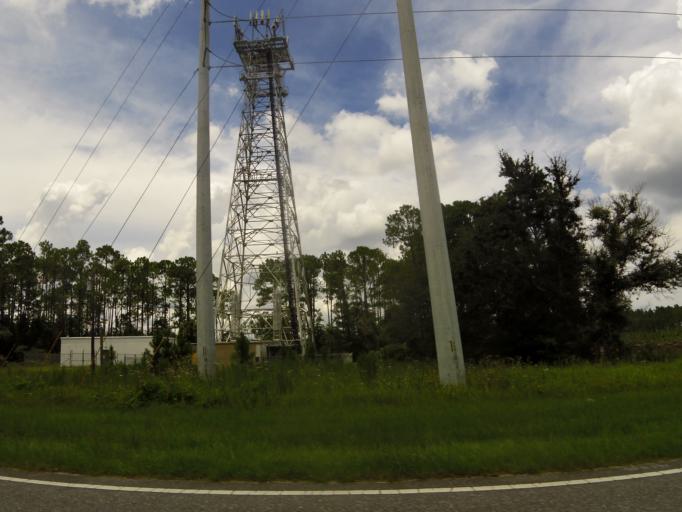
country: US
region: Florida
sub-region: Flagler County
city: Palm Coast
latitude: 29.6580
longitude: -81.2999
